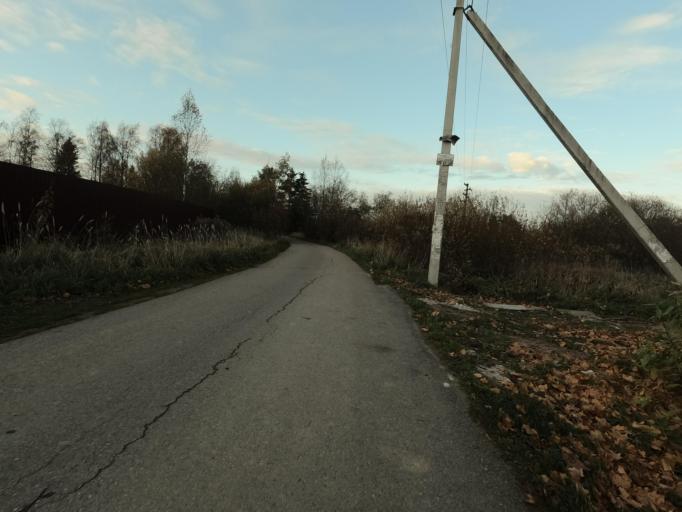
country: RU
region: Leningrad
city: Mga
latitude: 59.7749
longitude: 31.2121
